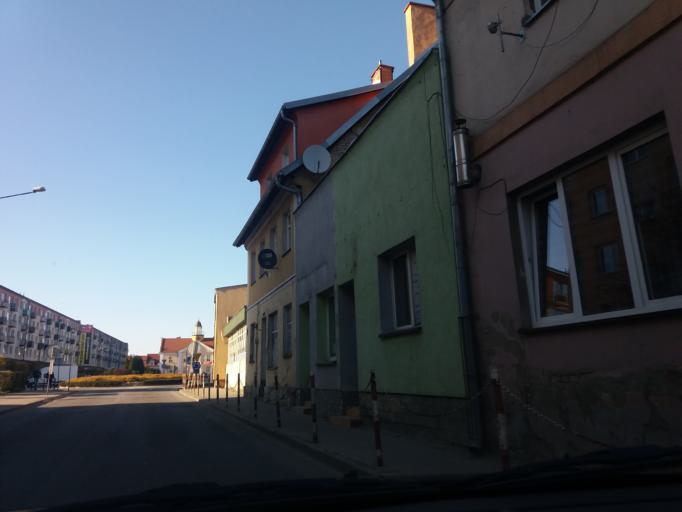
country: PL
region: Warmian-Masurian Voivodeship
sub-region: Powiat nidzicki
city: Nidzica
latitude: 53.3580
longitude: 20.4258
